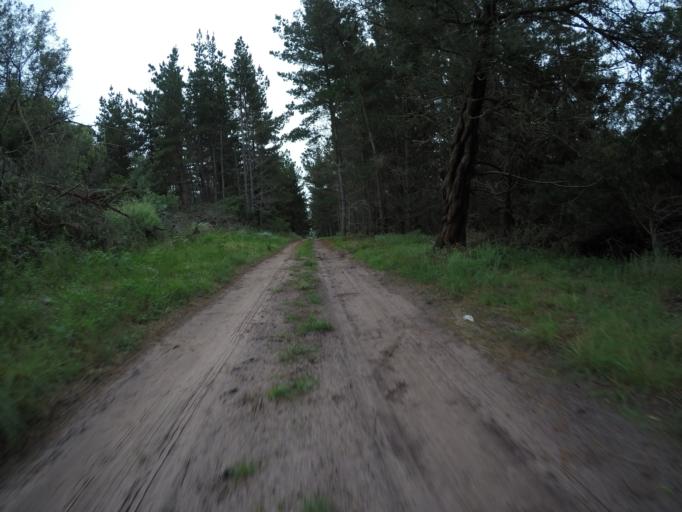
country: ZA
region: Western Cape
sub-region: Eden District Municipality
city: Knysna
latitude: -34.0093
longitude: 22.8086
